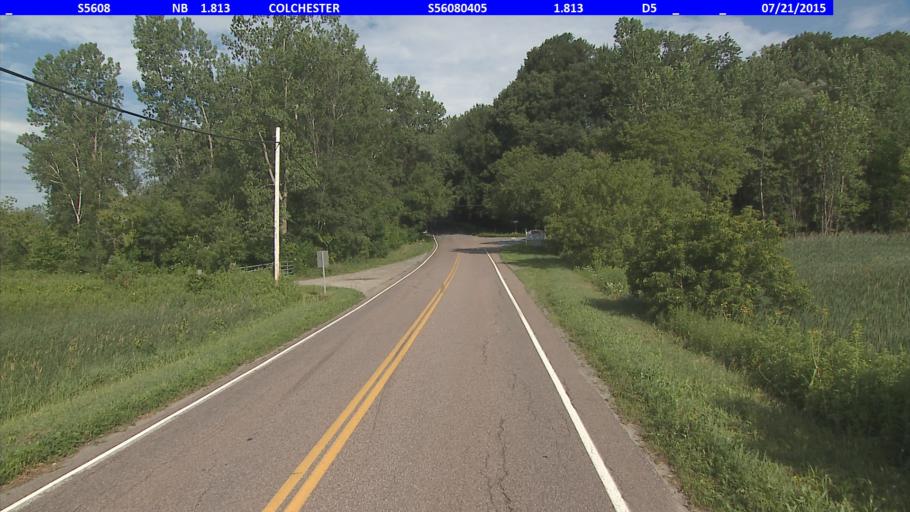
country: US
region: Vermont
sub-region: Chittenden County
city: Winooski
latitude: 44.5239
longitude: -73.2037
